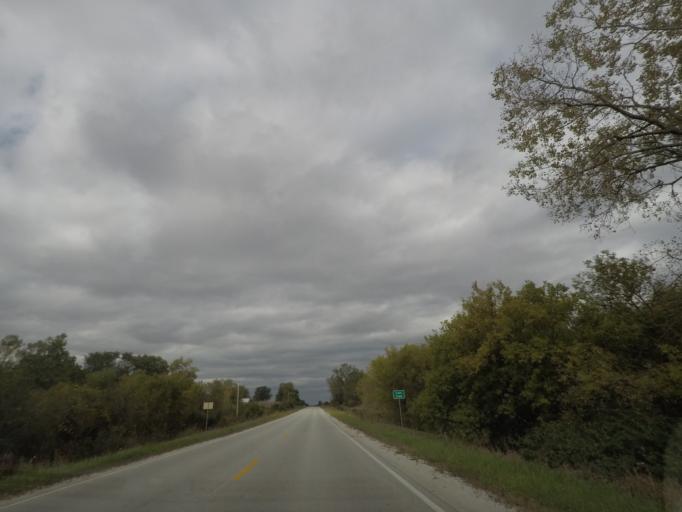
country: US
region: Iowa
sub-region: Story County
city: Huxley
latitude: 41.8673
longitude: -93.5316
